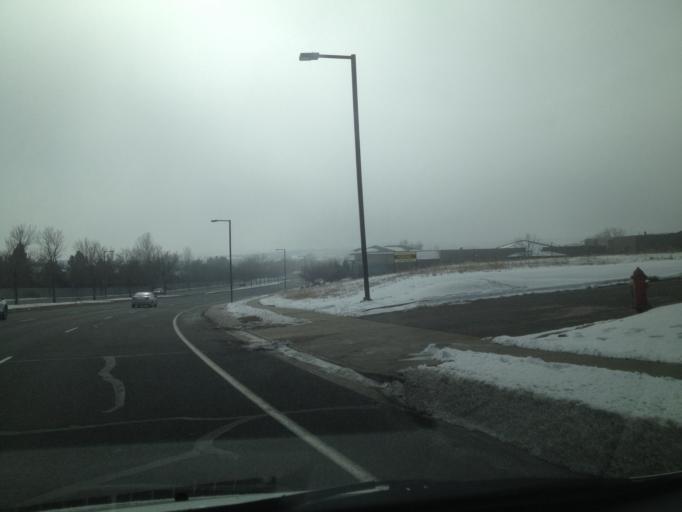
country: US
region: Colorado
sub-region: Boulder County
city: Superior
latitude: 39.9716
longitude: -105.1639
